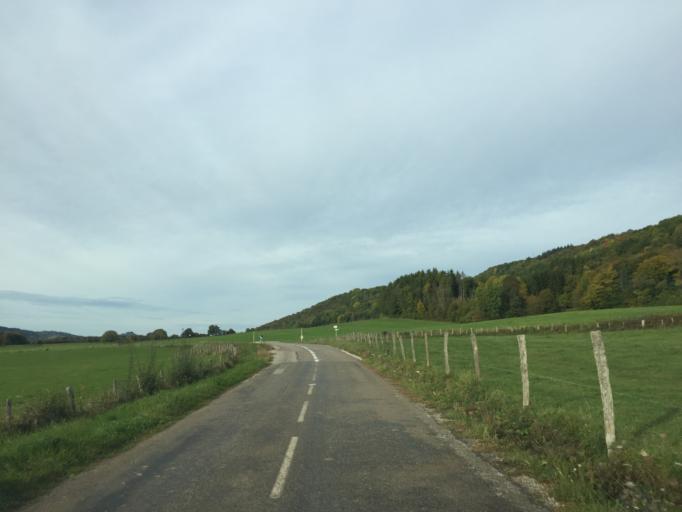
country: FR
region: Franche-Comte
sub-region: Departement du Jura
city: Orgelet
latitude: 46.5468
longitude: 5.5311
